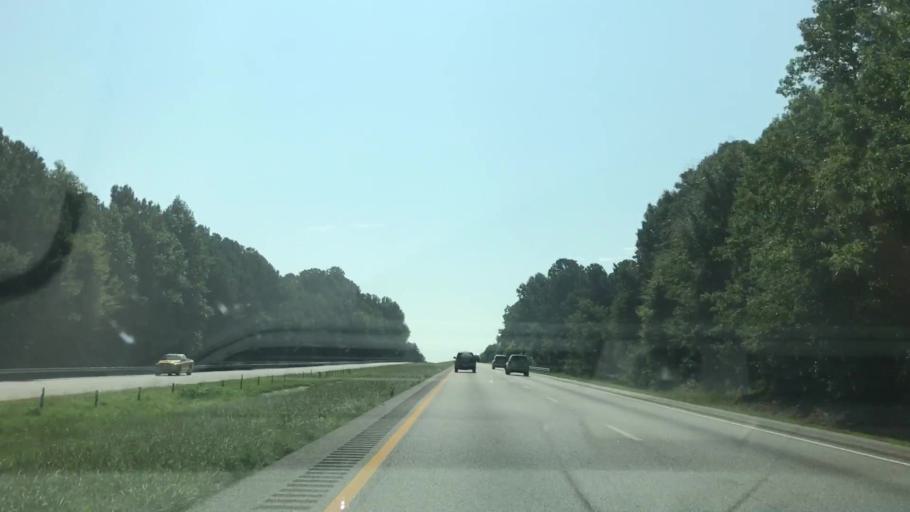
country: US
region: South Carolina
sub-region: Laurens County
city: Clinton
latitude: 34.4835
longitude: -81.8275
